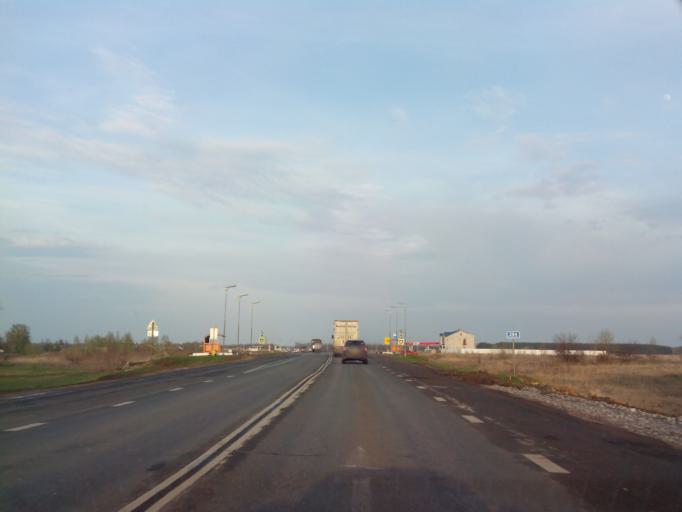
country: RU
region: Rjazan
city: Zarechnyy
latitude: 53.7523
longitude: 39.8038
